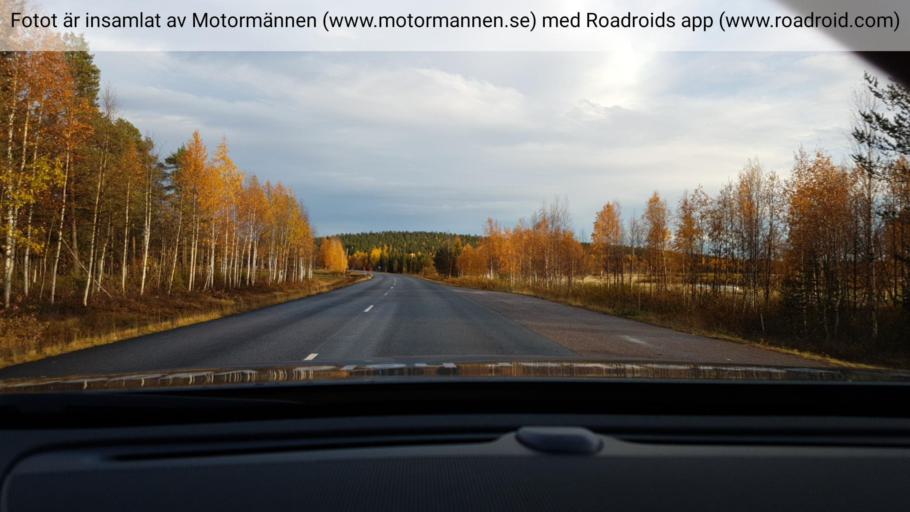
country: SE
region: Norrbotten
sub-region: Overkalix Kommun
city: OEverkalix
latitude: 66.9706
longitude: 22.6466
